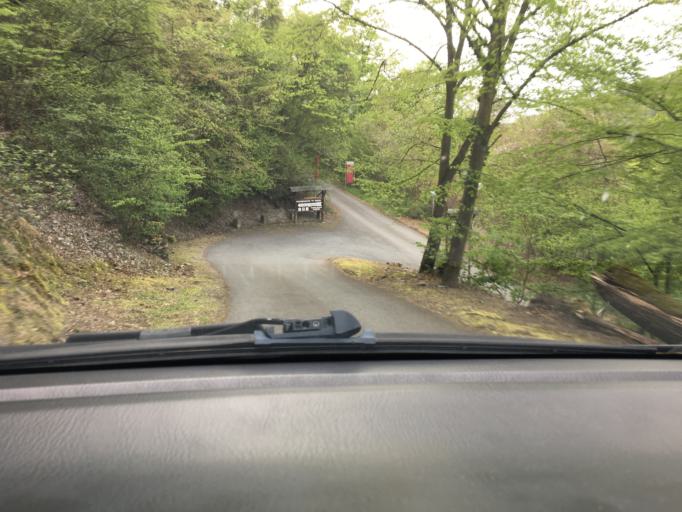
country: DE
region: Rheinland-Pfalz
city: Kamp-Bornhofen
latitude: 50.2131
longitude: 7.6362
